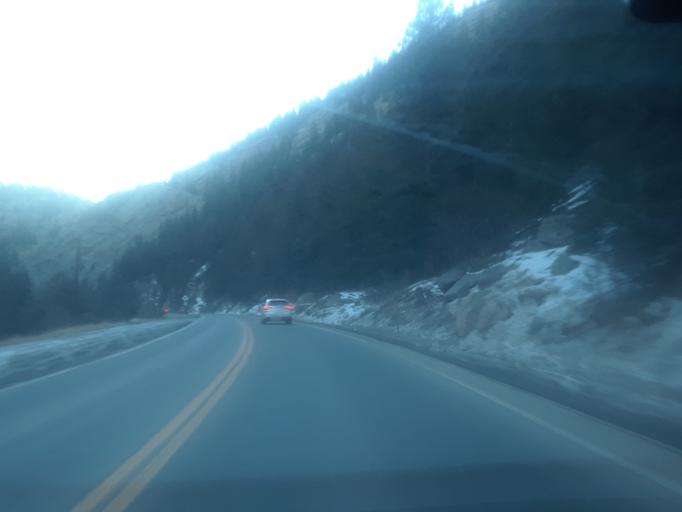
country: US
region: Colorado
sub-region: Clear Creek County
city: Idaho Springs
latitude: 39.7366
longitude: -105.4179
